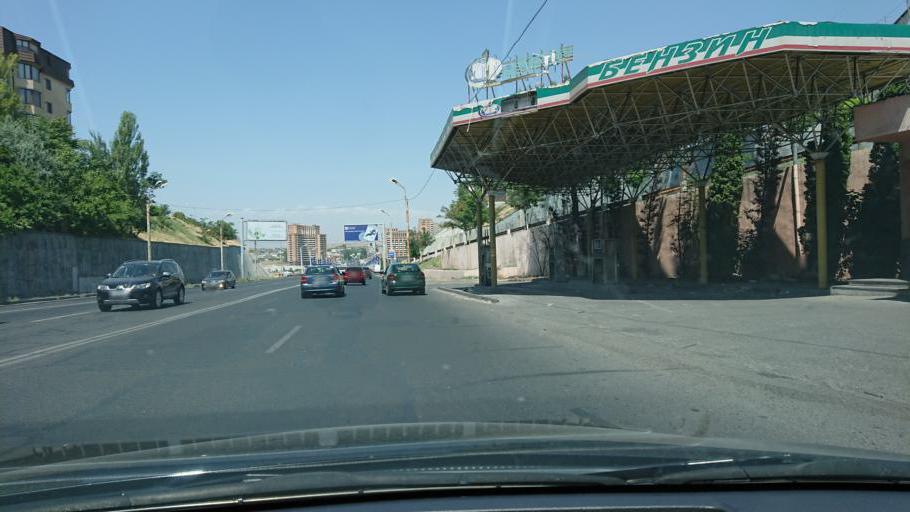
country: AM
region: Yerevan
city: Yerevan
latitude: 40.2065
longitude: 44.4963
